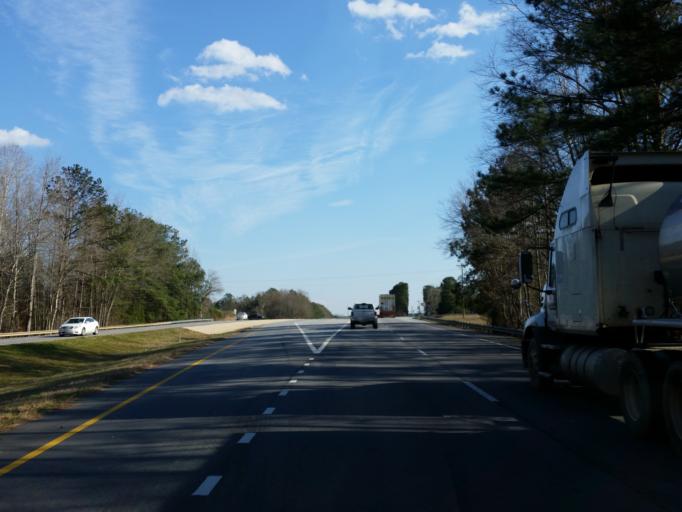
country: US
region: Georgia
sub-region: Spalding County
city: East Griffin
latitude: 33.1434
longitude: -84.2416
